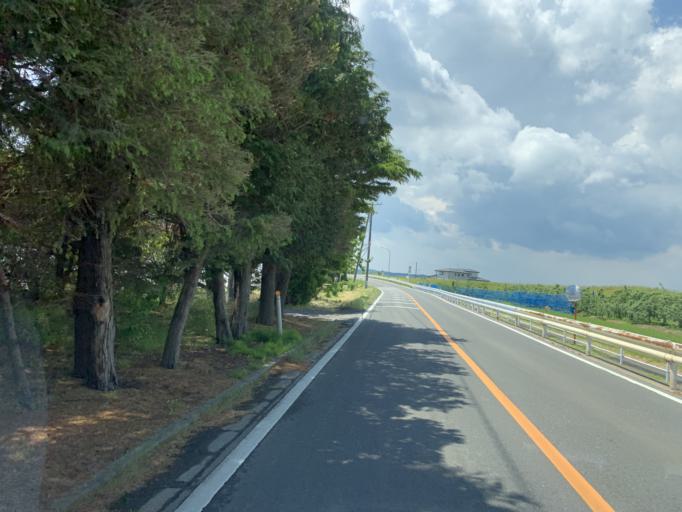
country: JP
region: Miyagi
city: Matsushima
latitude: 38.4607
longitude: 141.0877
